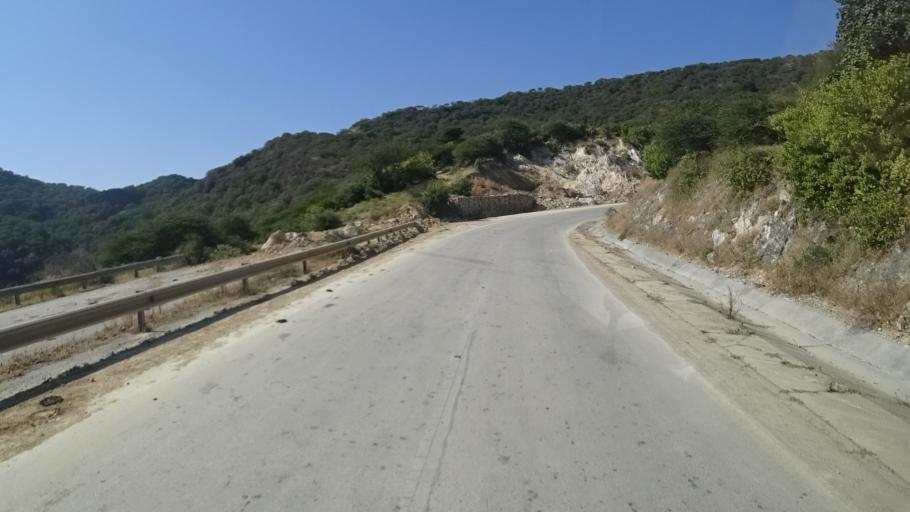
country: OM
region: Zufar
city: Salalah
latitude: 17.0578
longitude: 54.6100
